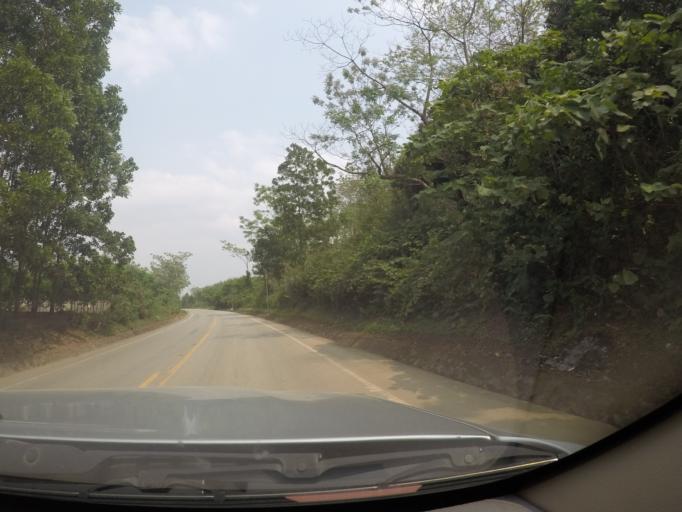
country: VN
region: Thanh Hoa
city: Thi Tran Yen Cat
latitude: 19.4778
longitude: 105.4003
